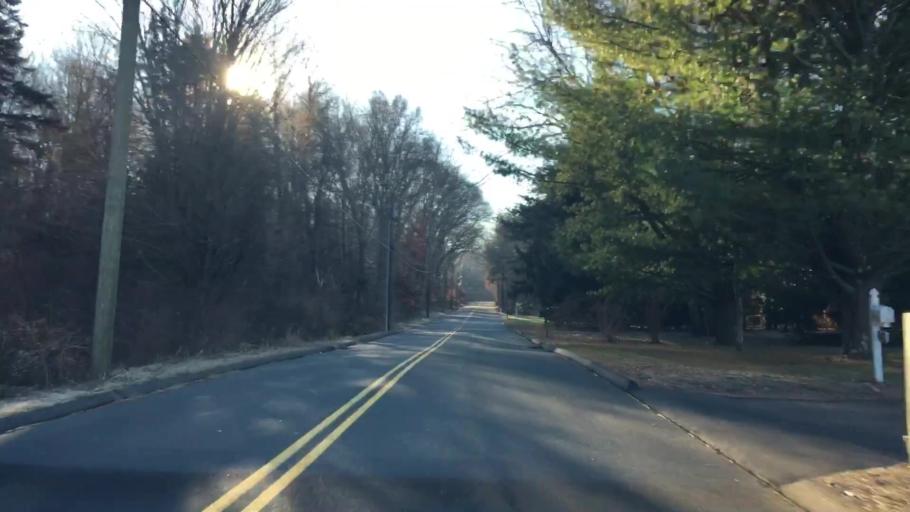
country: US
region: Connecticut
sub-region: New Haven County
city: Cheshire Village
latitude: 41.5602
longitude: -72.8724
